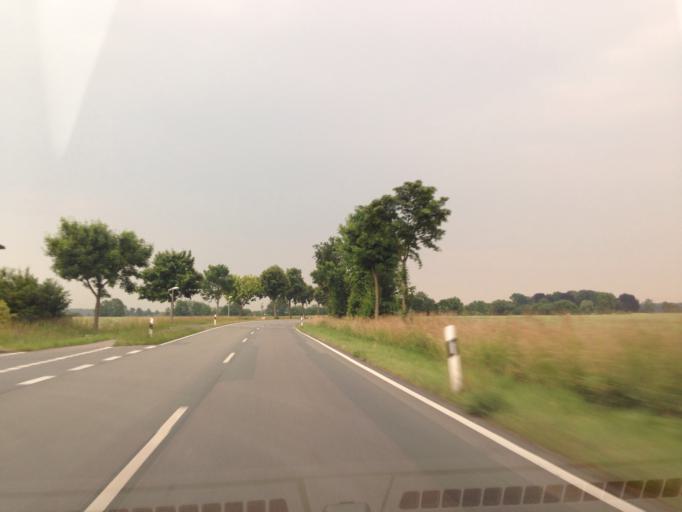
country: DE
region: North Rhine-Westphalia
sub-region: Regierungsbezirk Munster
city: Havixbeck
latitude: 51.9636
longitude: 7.4237
